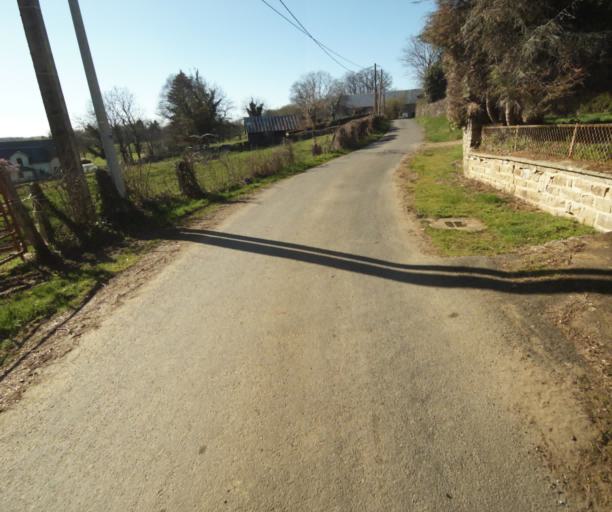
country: FR
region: Limousin
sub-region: Departement de la Correze
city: Chamboulive
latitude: 45.3937
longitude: 1.6676
